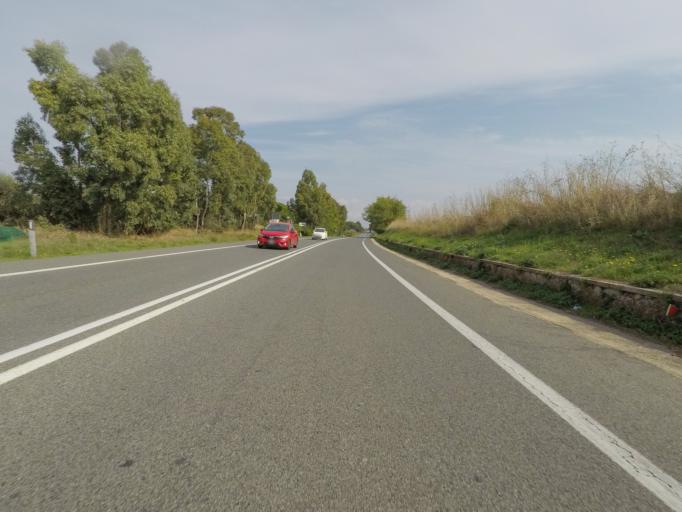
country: IT
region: Tuscany
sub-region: Provincia di Grosseto
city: Capalbio
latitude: 42.4152
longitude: 11.3413
